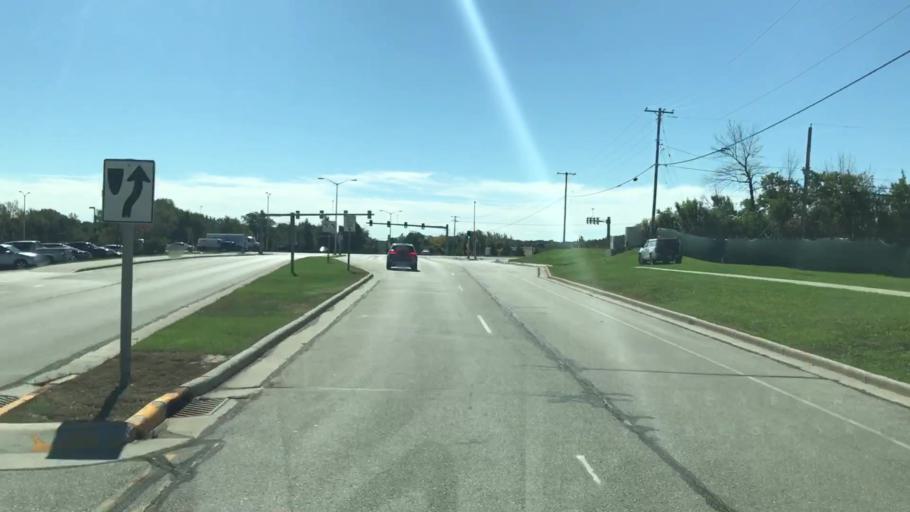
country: US
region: Wisconsin
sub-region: Waukesha County
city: Brookfield
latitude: 43.0915
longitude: -88.1256
